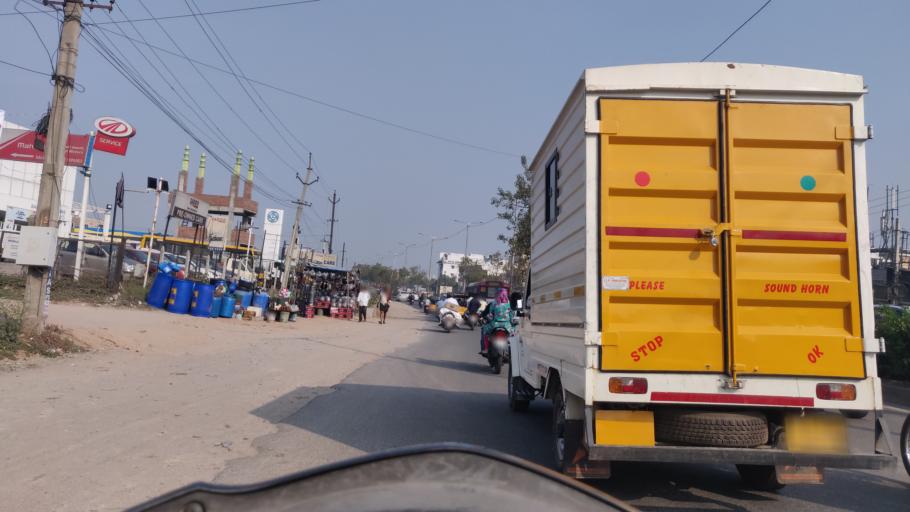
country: IN
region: Telangana
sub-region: Rangareddi
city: Uppal Kalan
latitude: 17.4016
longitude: 78.5727
